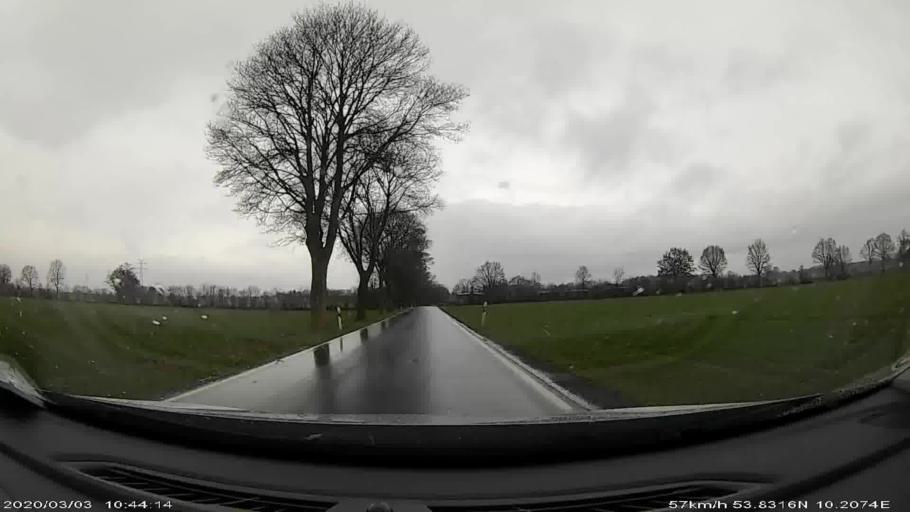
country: DE
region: Schleswig-Holstein
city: Seth
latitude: 53.8340
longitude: 10.2047
